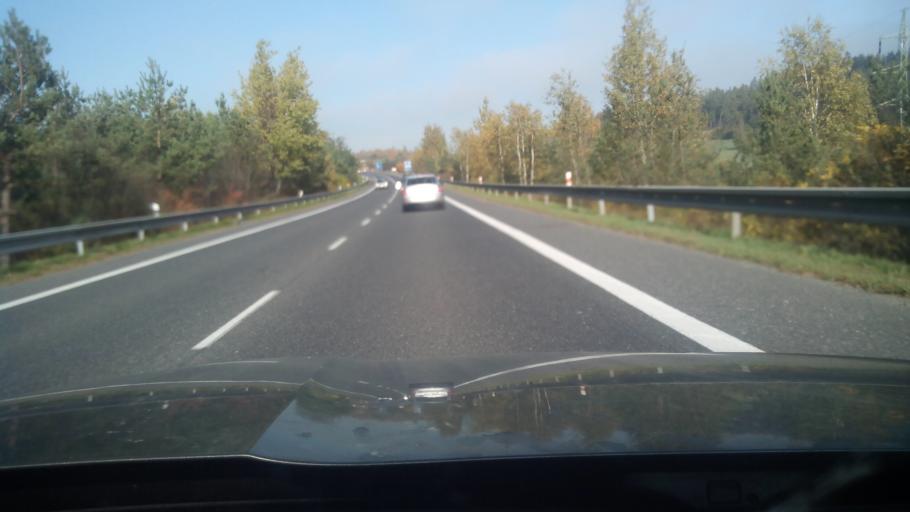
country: CZ
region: Central Bohemia
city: Milin
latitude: 49.6318
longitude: 14.0516
